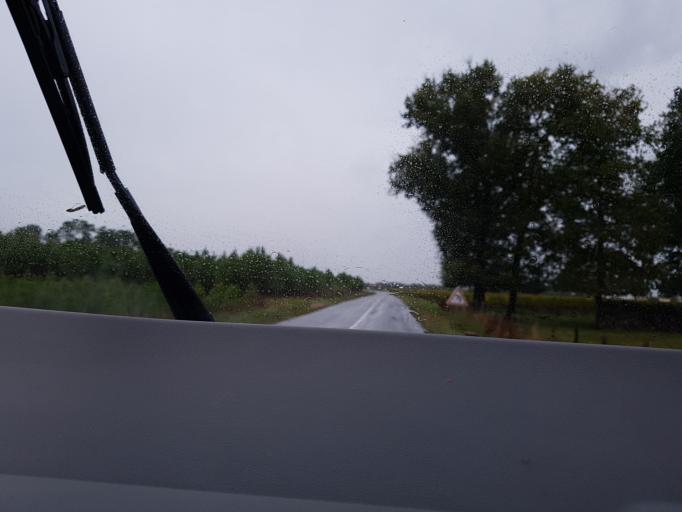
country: FR
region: Aquitaine
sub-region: Departement de la Gironde
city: Saint-Savin
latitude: 45.1784
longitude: -0.4504
